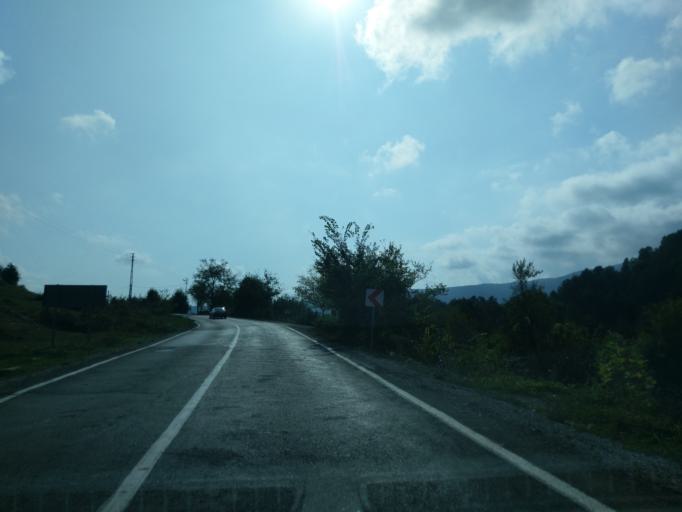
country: TR
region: Sinop
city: Ayancik
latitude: 41.8789
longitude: 34.5286
